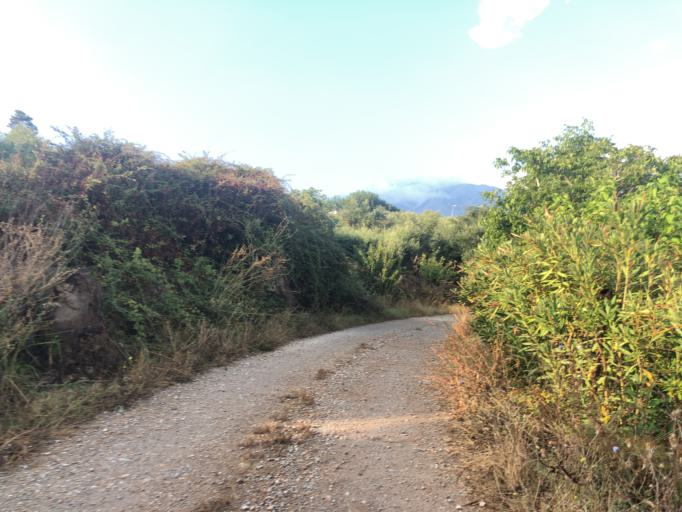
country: GR
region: Crete
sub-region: Nomos Chanias
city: Georgioupolis
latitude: 35.3460
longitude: 24.3133
